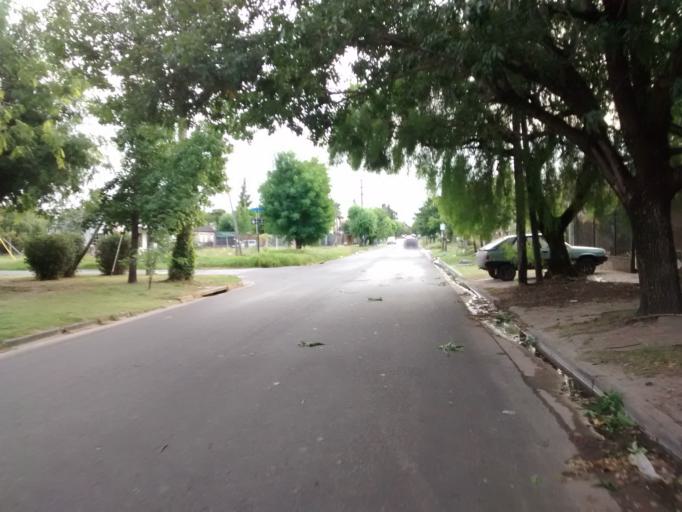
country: AR
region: Buenos Aires
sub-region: Partido de La Plata
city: La Plata
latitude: -34.8734
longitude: -58.0590
